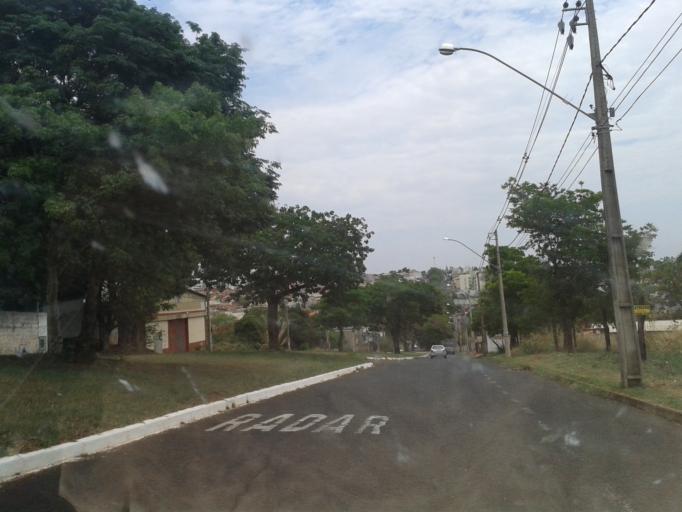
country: BR
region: Minas Gerais
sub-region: Uberlandia
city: Uberlandia
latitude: -18.9185
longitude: -48.3105
